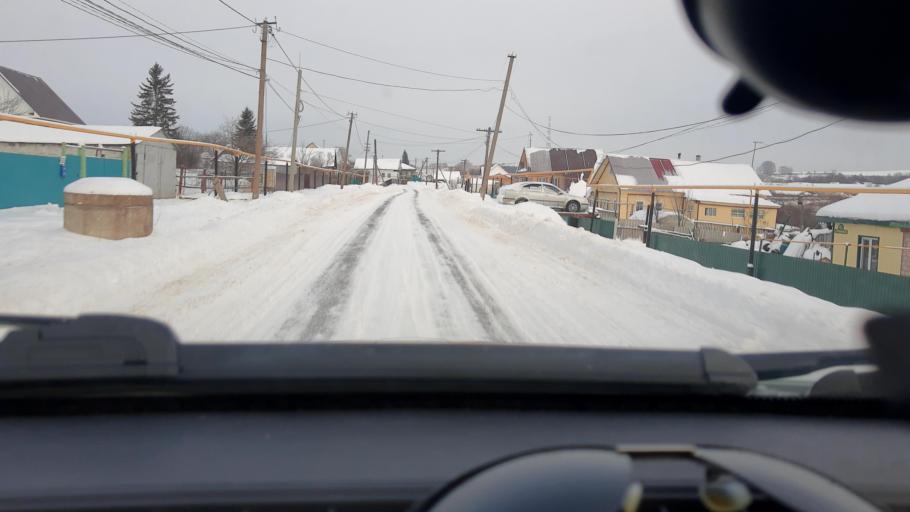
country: RU
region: Bashkortostan
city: Yazykovo
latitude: 55.0305
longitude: 56.2234
